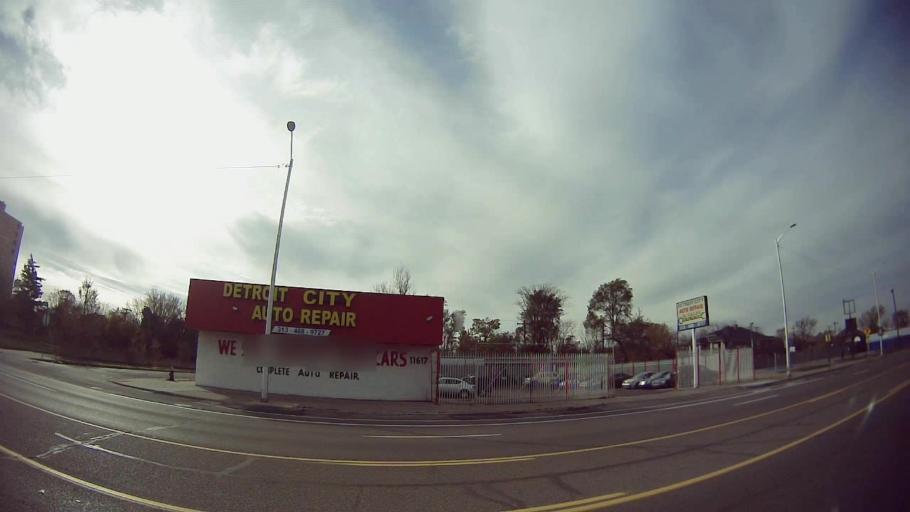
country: US
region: Michigan
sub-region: Wayne County
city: Highland Park
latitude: 42.3792
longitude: -83.1236
